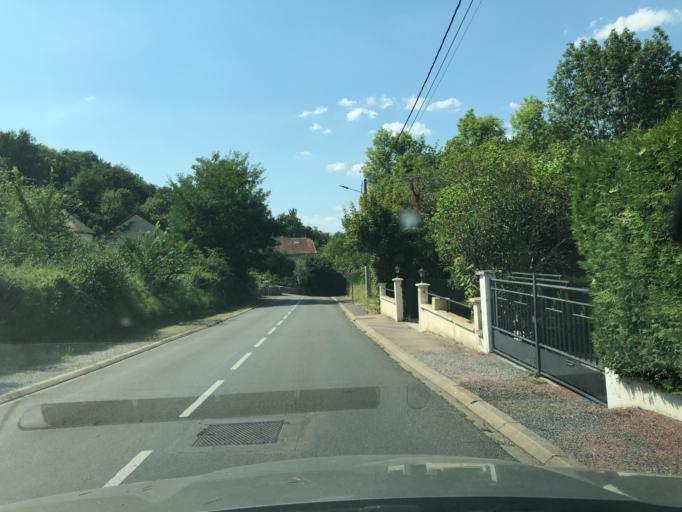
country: FR
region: Auvergne
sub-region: Departement de l'Allier
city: Cusset
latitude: 46.1271
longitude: 3.4651
